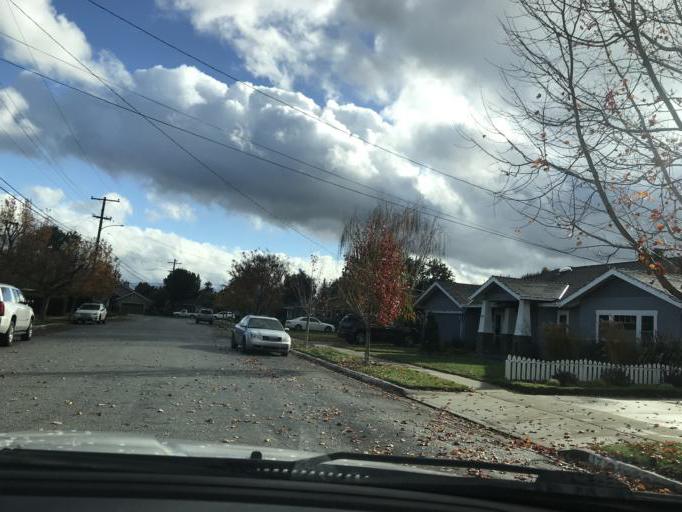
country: US
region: California
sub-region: Santa Clara County
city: Buena Vista
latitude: 37.2999
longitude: -121.9162
